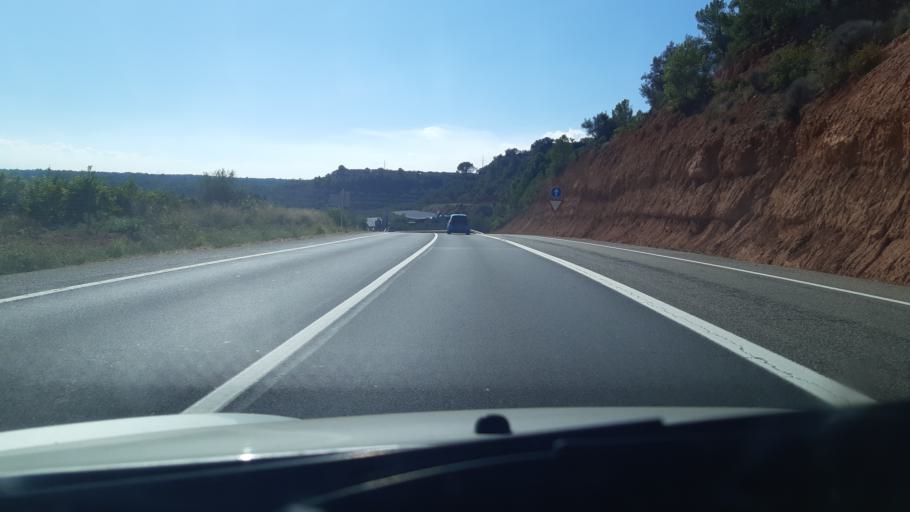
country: ES
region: Catalonia
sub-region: Provincia de Tarragona
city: Tivenys
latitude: 40.9116
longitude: 0.4847
